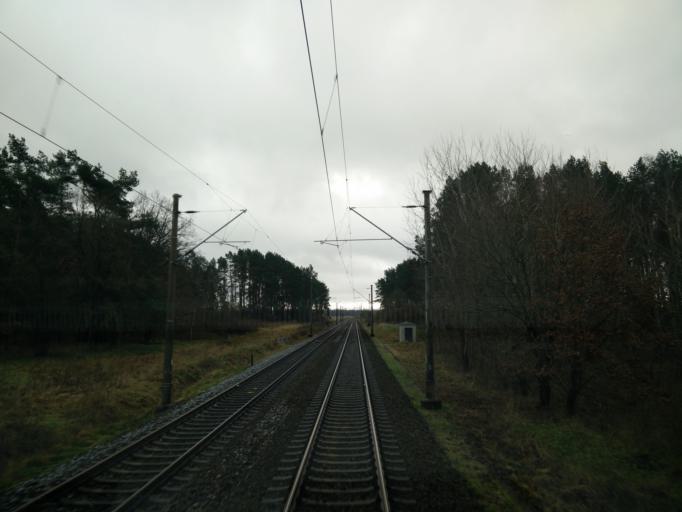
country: DE
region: Mecklenburg-Vorpommern
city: Ludwigslust
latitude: 53.3962
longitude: 11.4724
